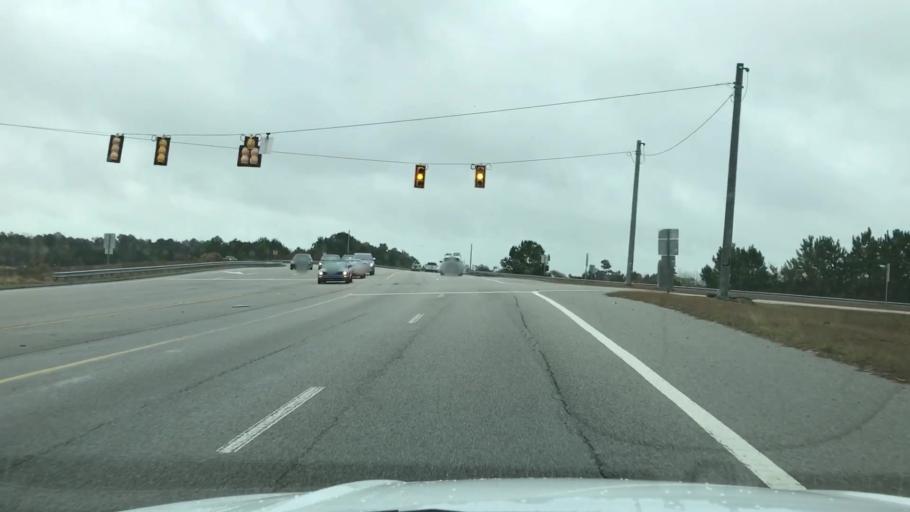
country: US
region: South Carolina
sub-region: Horry County
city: Myrtle Beach
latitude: 33.7564
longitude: -78.8552
